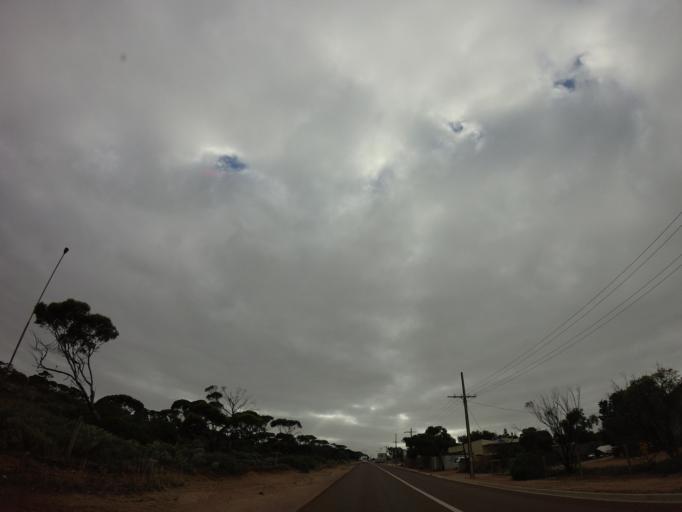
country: AU
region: South Australia
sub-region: Ceduna
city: Ceduna
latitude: -32.1218
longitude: 133.6807
